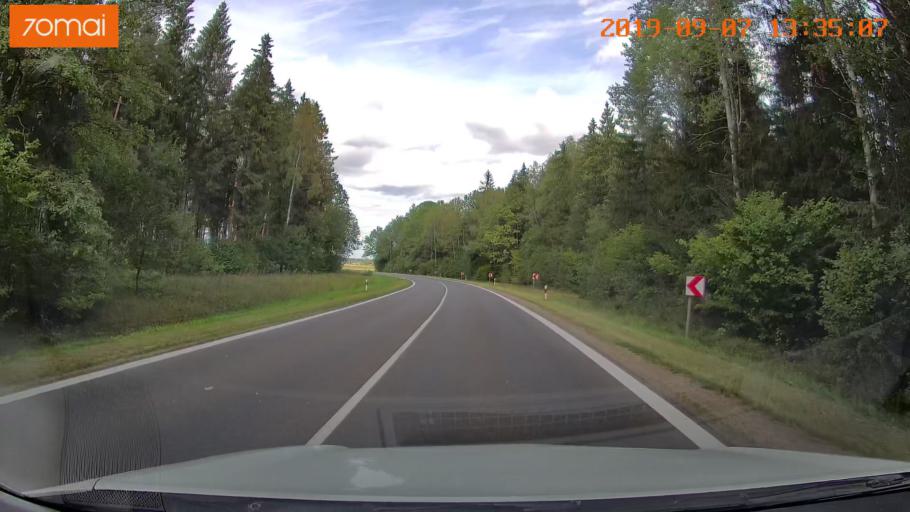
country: LT
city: Skaidiskes
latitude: 54.5063
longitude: 25.3207
